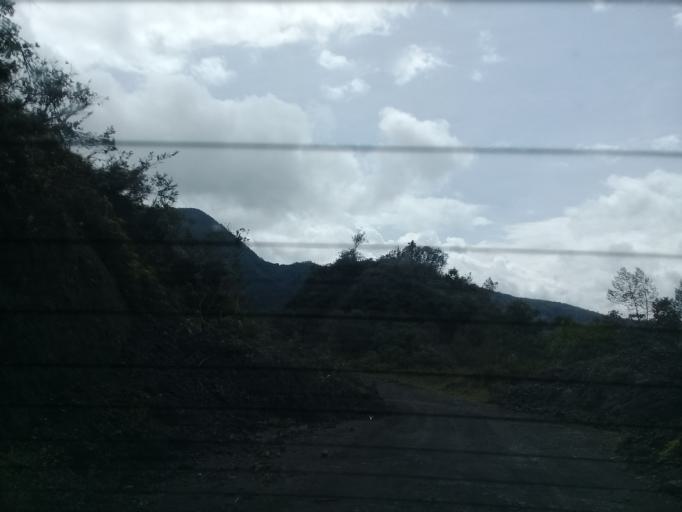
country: CO
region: Cundinamarca
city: Gachala
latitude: 4.7027
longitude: -73.4464
